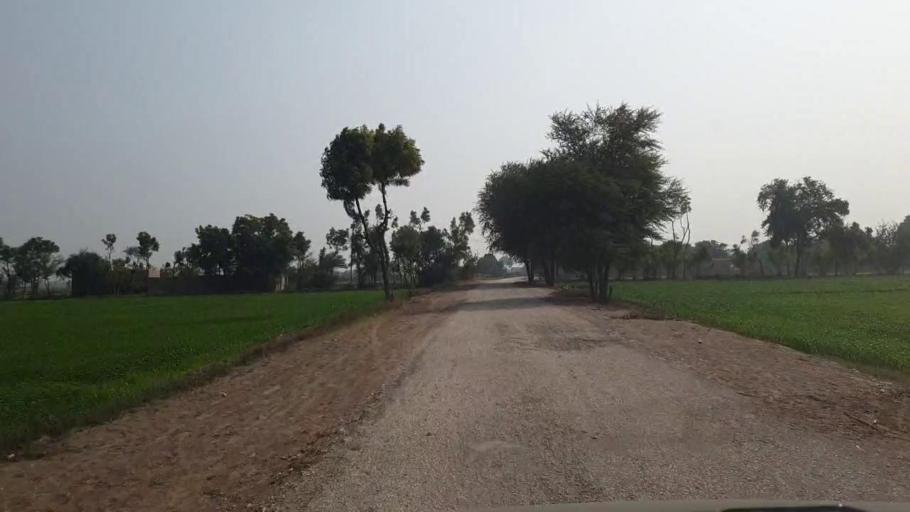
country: PK
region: Sindh
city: Bhit Shah
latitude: 25.8510
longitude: 68.5012
